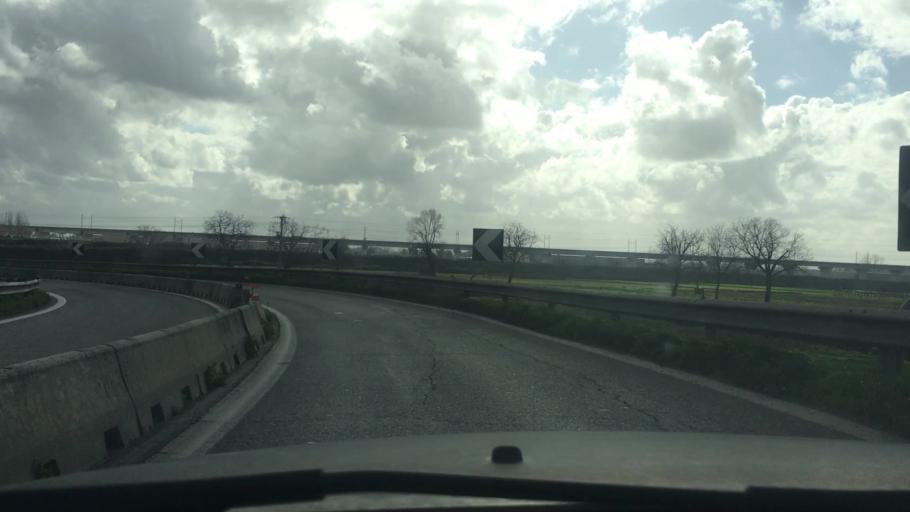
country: IT
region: Campania
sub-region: Provincia di Caserta
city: Marcianise
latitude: 41.0193
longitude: 14.3202
